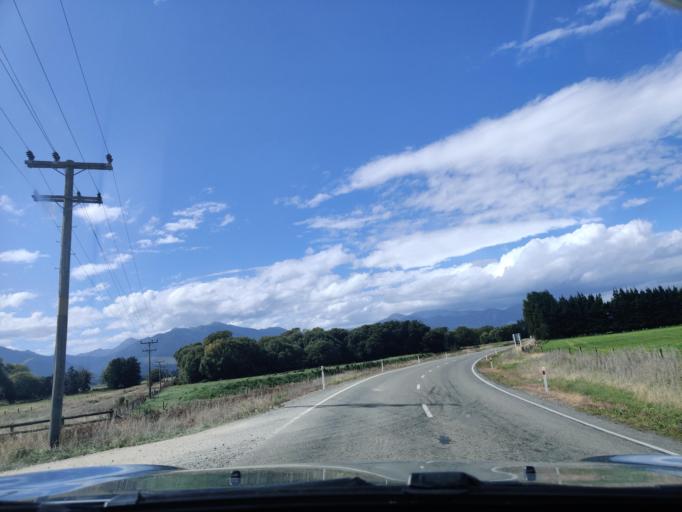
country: NZ
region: Canterbury
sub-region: Hurunui District
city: Amberley
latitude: -42.5641
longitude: 172.7944
